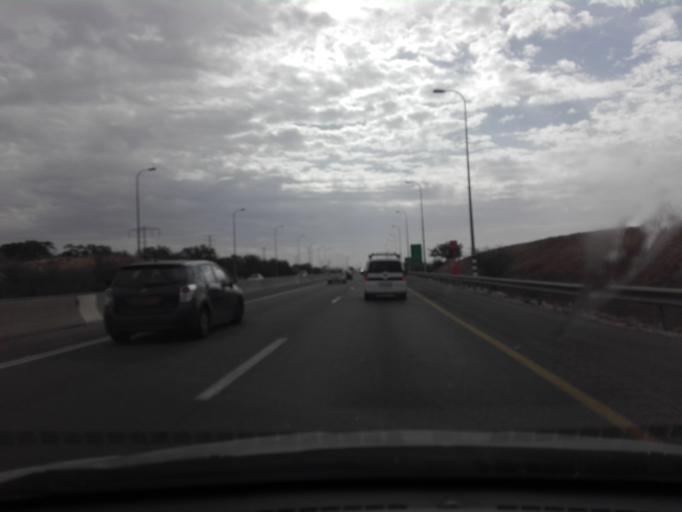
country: IL
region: Southern District
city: Lehavim
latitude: 31.3189
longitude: 34.7872
